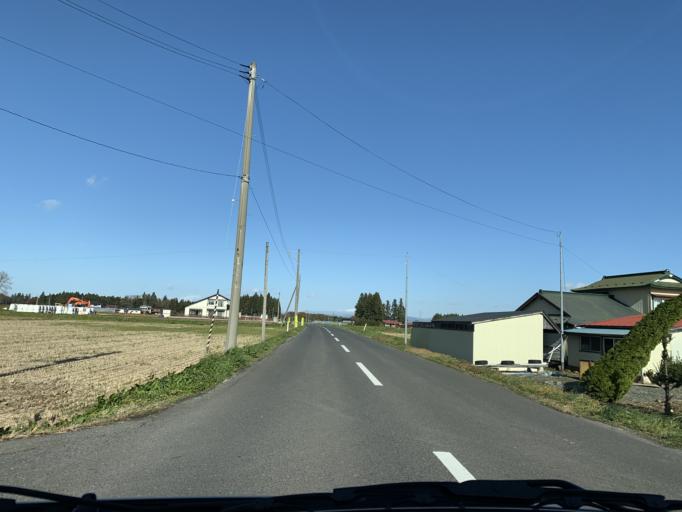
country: JP
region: Iwate
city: Mizusawa
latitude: 39.0748
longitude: 141.1192
